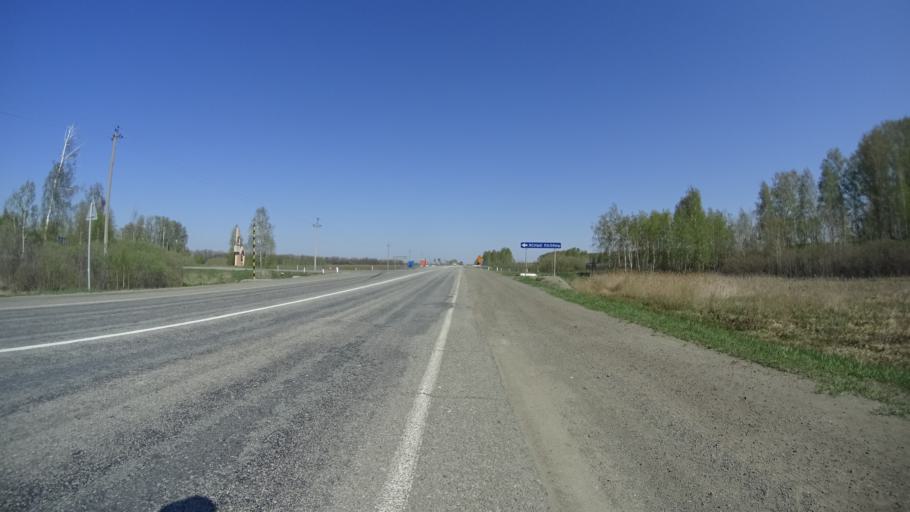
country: RU
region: Chelyabinsk
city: Troitsk
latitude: 54.1865
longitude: 61.4341
